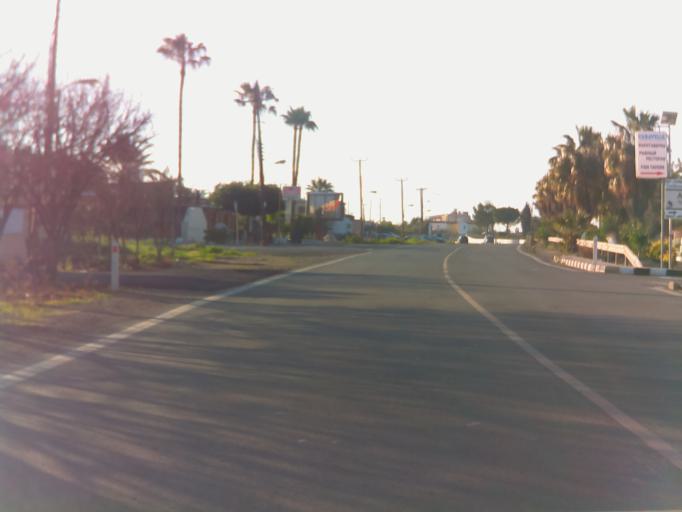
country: CY
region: Pafos
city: Kissonerga
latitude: 34.8079
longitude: 32.3968
